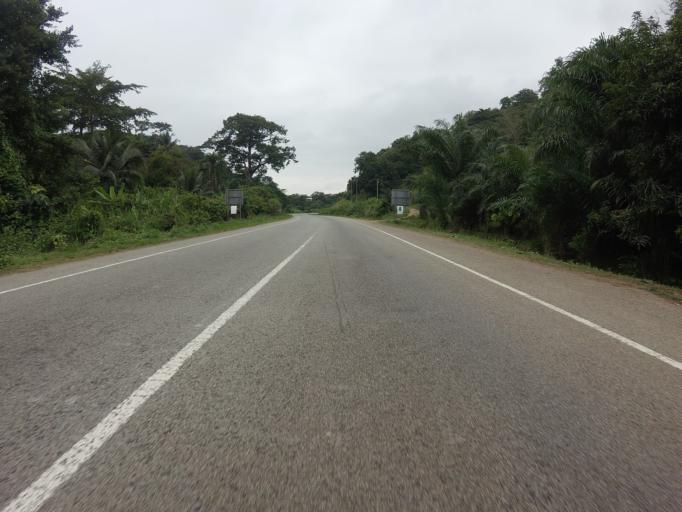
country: GH
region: Volta
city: Ho
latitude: 6.6960
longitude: 0.4812
